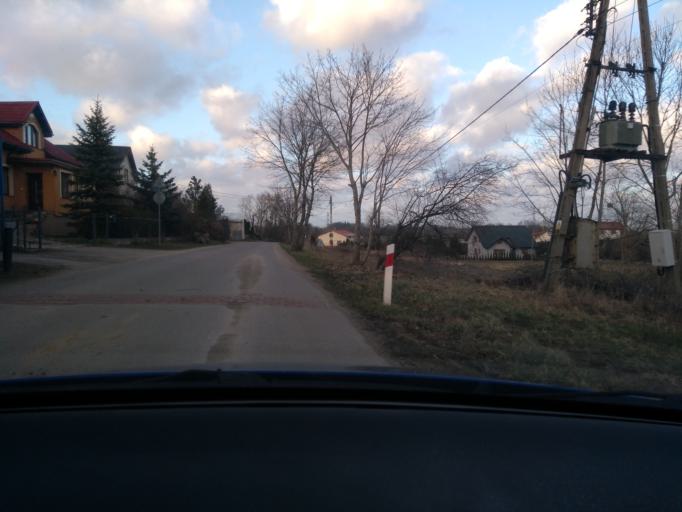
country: PL
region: Pomeranian Voivodeship
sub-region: Powiat kartuski
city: Przodkowo
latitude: 54.4168
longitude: 18.2801
